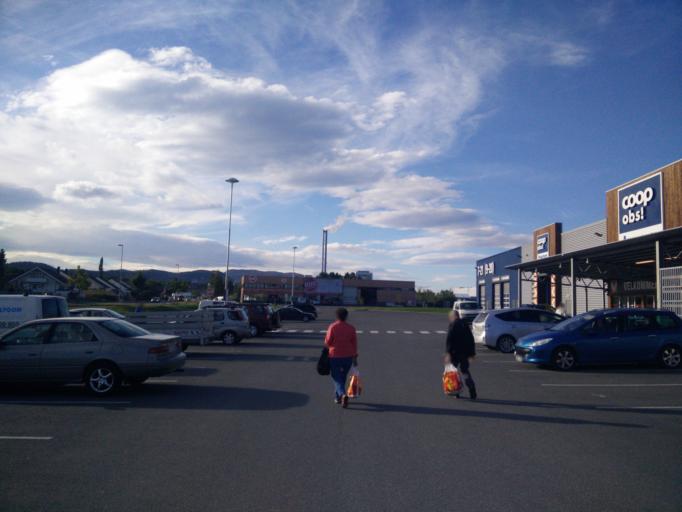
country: NO
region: Sor-Trondelag
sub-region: Trondheim
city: Trondheim
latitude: 63.3538
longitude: 10.3746
